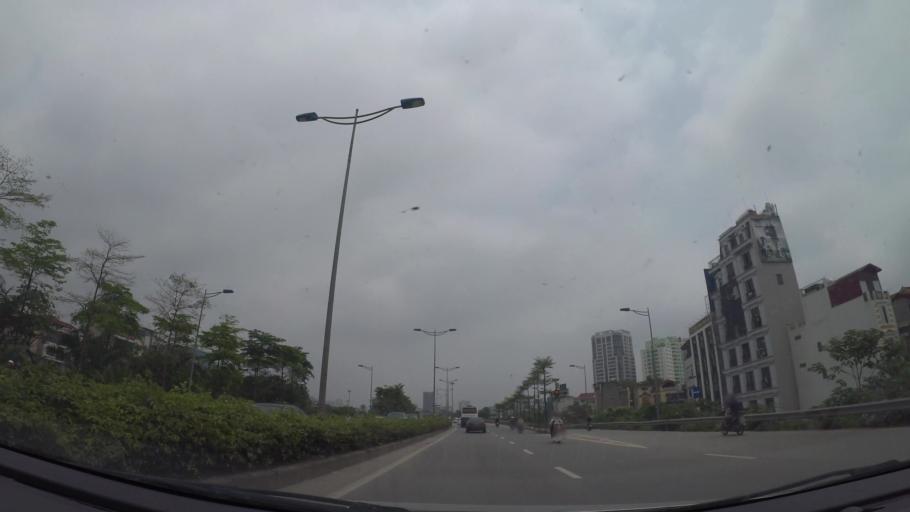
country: VN
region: Ha Noi
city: Cau Giay
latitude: 21.0438
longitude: 105.8061
